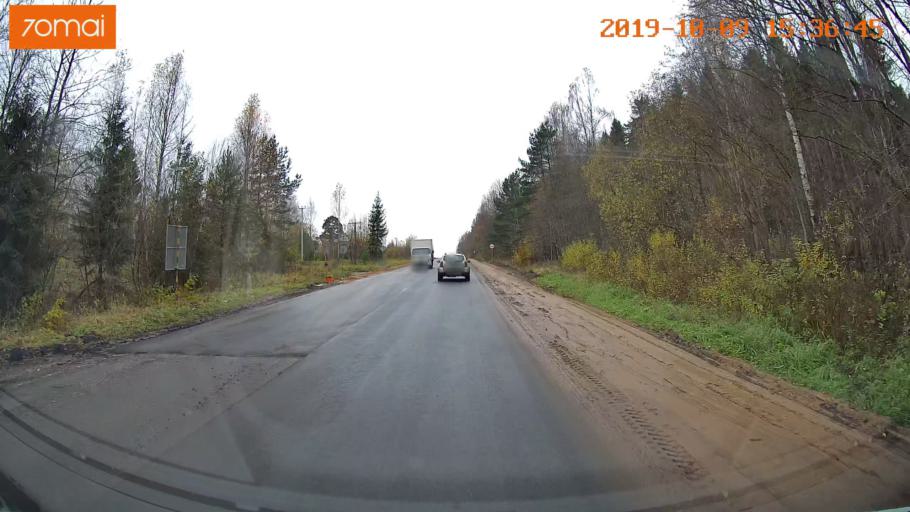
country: RU
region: Kostroma
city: Oktyabr'skiy
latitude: 57.9223
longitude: 41.2076
